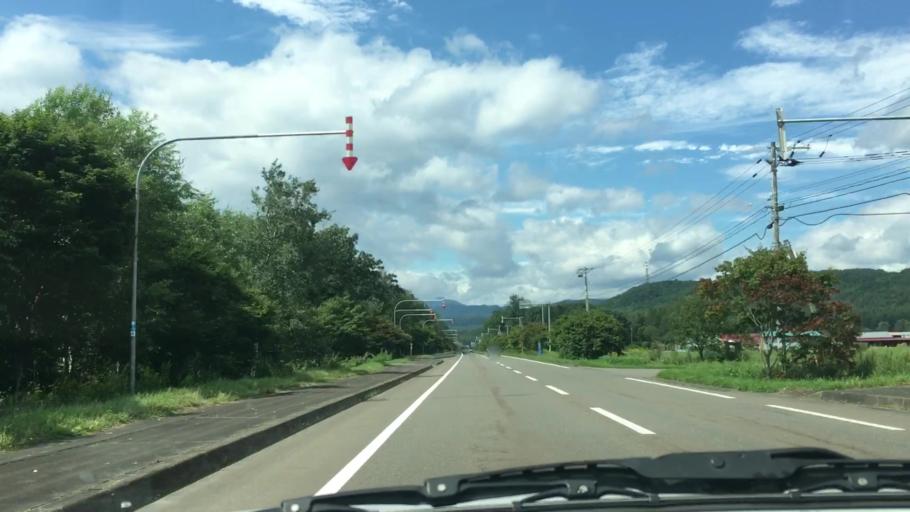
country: JP
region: Hokkaido
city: Otofuke
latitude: 43.3144
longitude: 143.3060
